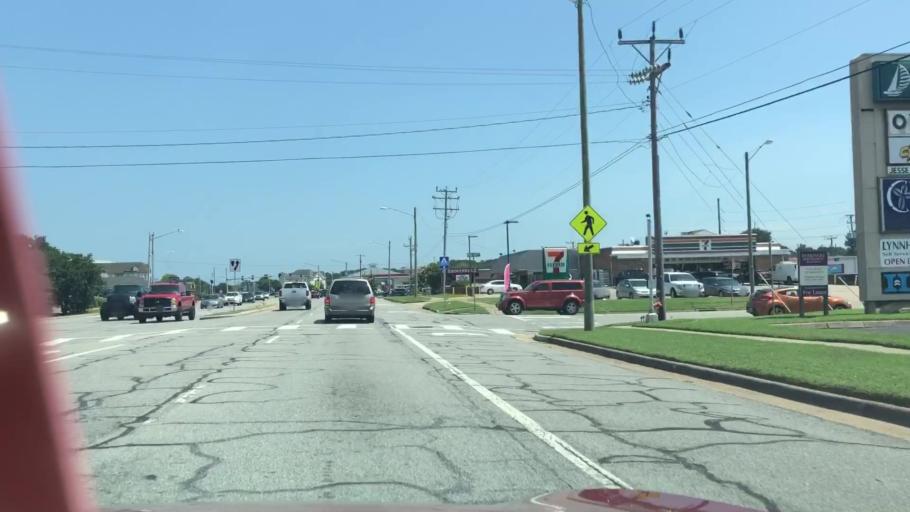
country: US
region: Virginia
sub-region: City of Virginia Beach
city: Virginia Beach
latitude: 36.9108
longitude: -76.0741
